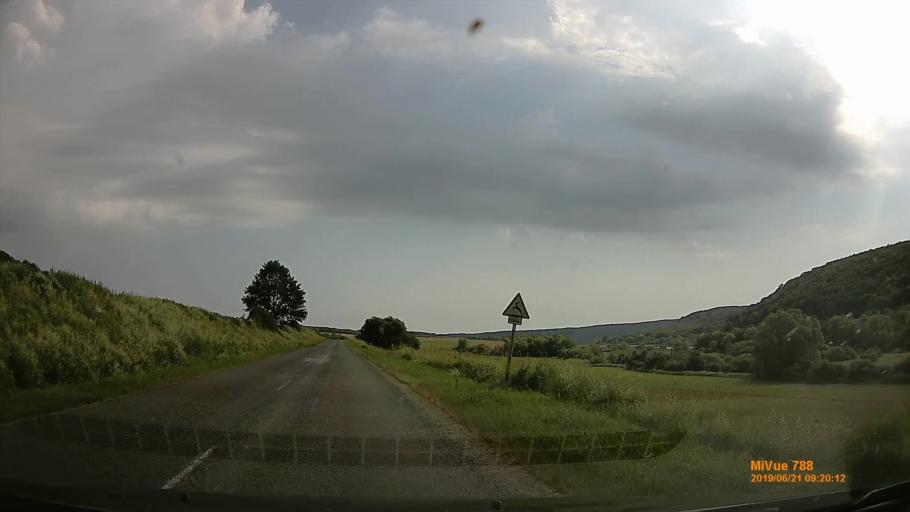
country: HU
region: Somogy
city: Taszar
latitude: 46.2327
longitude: 17.8699
